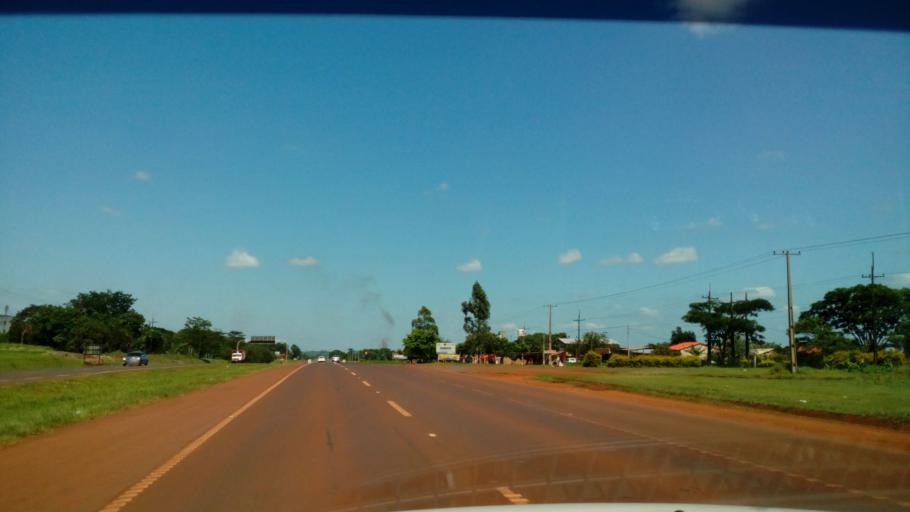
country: PY
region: Alto Parana
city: Colonia Yguazu
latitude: -25.4865
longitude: -54.8625
